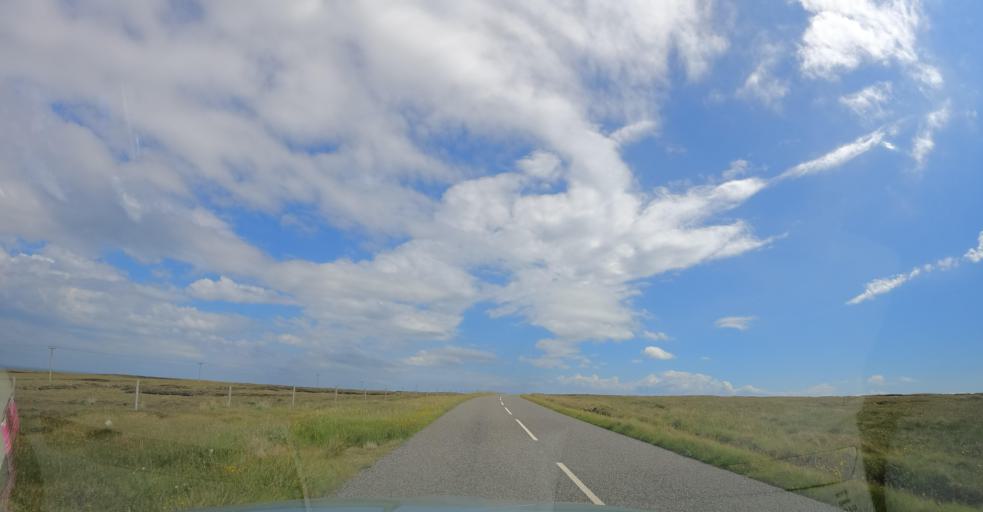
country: GB
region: Scotland
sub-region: Eilean Siar
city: Isle of Lewis
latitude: 58.4581
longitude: -6.3363
